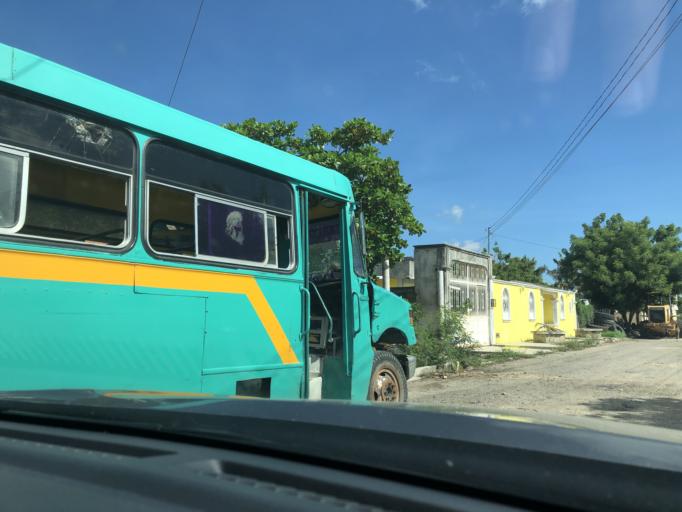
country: MX
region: Oaxaca
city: San Jeronimo Ixtepec
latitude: 16.5560
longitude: -95.1041
